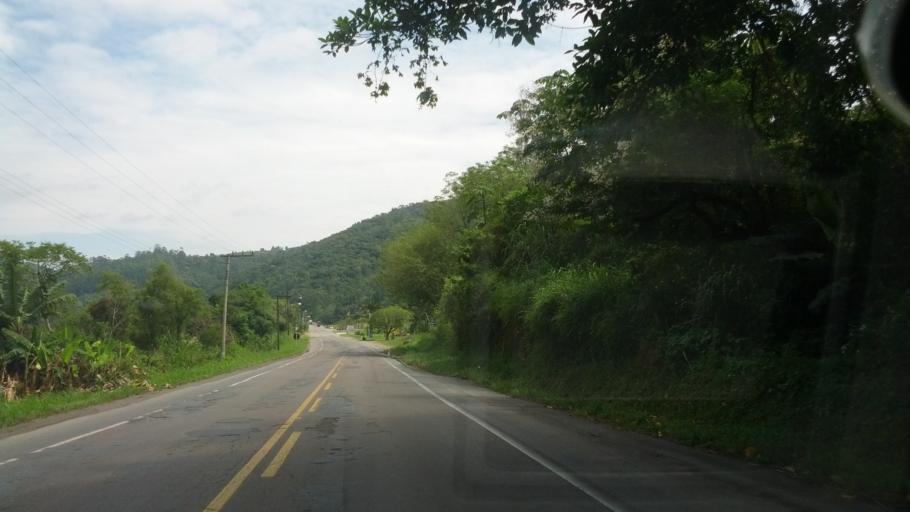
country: BR
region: Santa Catarina
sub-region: Ibirama
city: Ibirama
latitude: -27.0848
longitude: -49.4806
